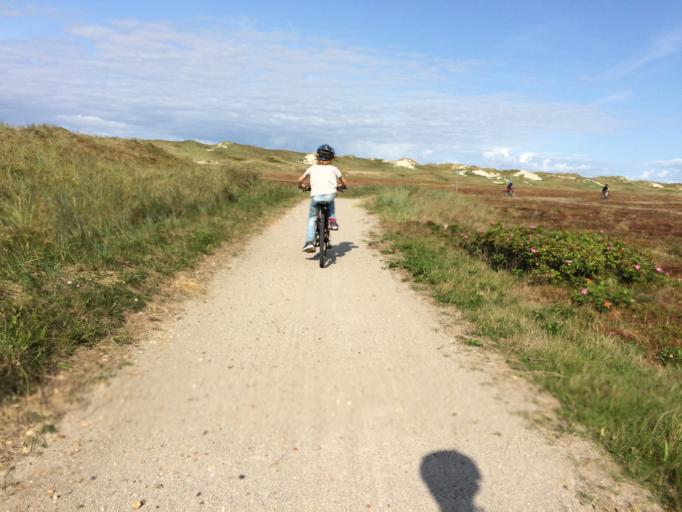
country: DK
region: Central Jutland
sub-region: Ringkobing-Skjern Kommune
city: Hvide Sande
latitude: 55.9023
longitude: 8.1582
